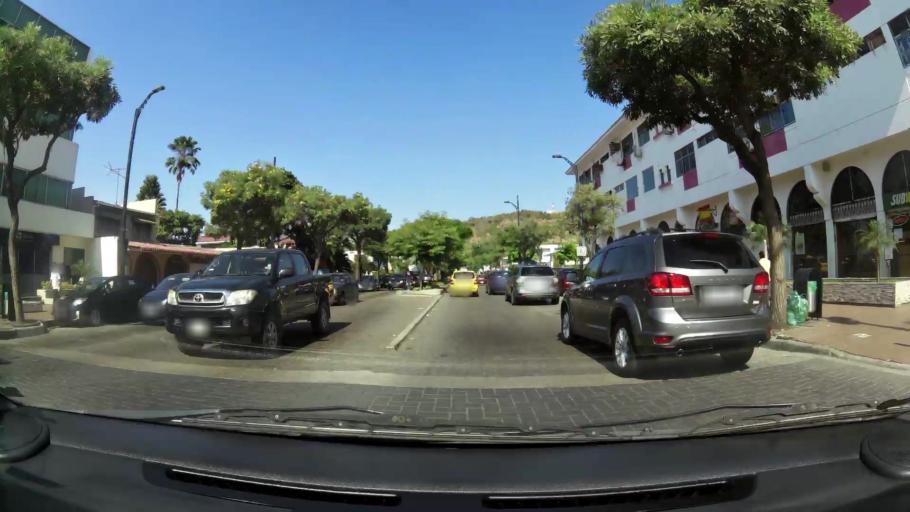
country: EC
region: Guayas
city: Guayaquil
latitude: -2.1699
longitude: -79.9099
